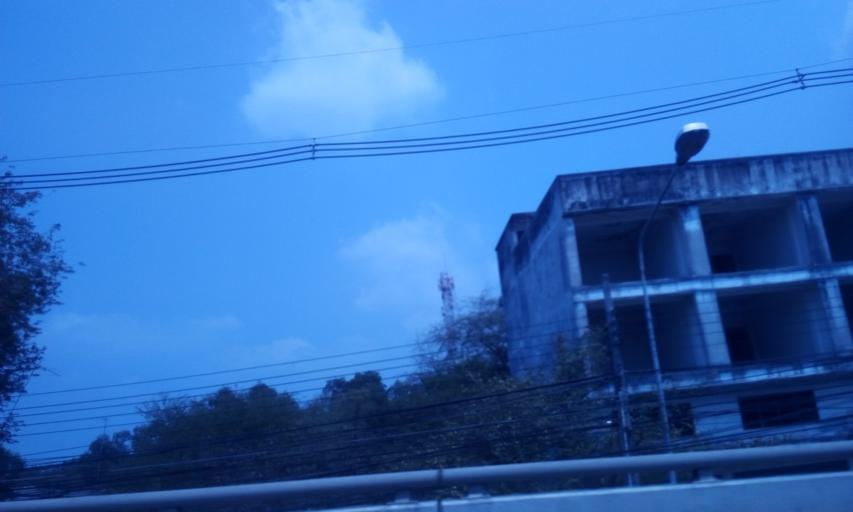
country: TH
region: Chachoengsao
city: Chachoengsao
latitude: 13.6862
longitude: 101.0782
